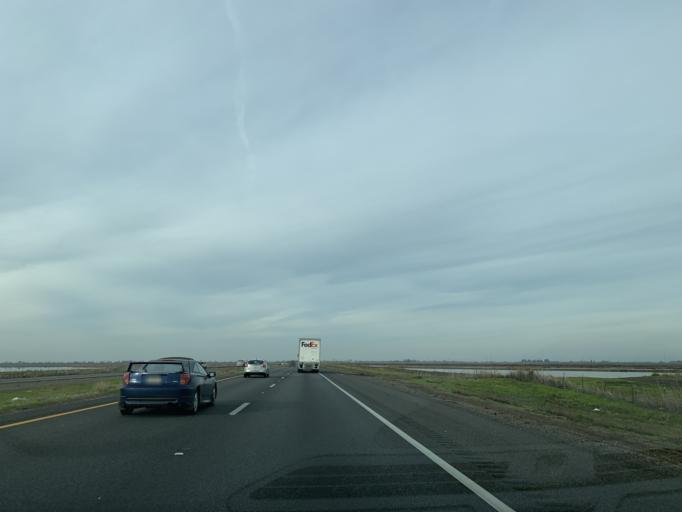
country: US
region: California
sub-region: Sacramento County
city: Elverta
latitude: 38.7900
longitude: -121.5435
